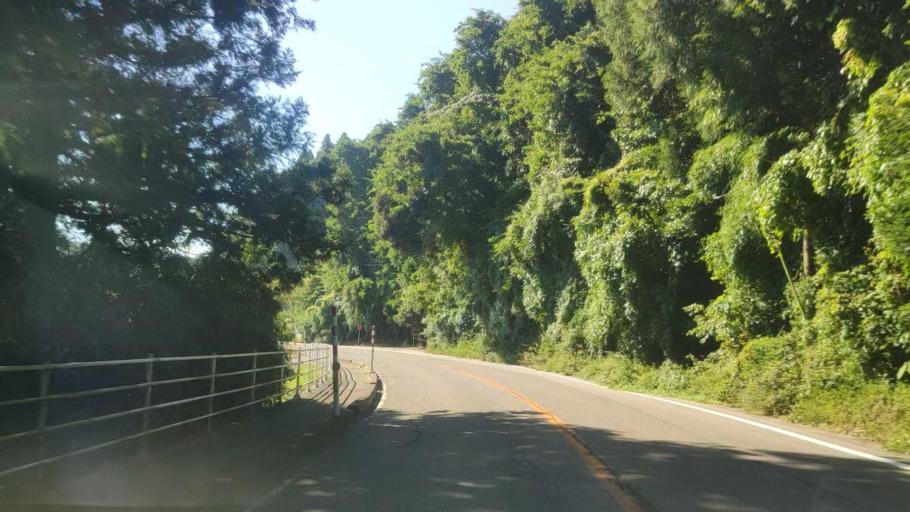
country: JP
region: Ishikawa
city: Nanao
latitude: 37.2569
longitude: 137.0861
